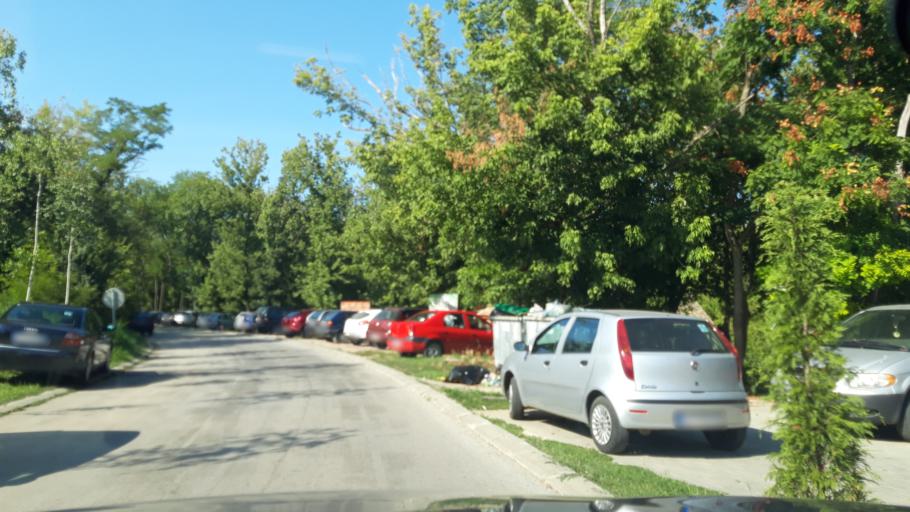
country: RS
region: Autonomna Pokrajina Vojvodina
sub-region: Sremski Okrug
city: Ruma
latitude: 45.0344
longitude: 19.8190
